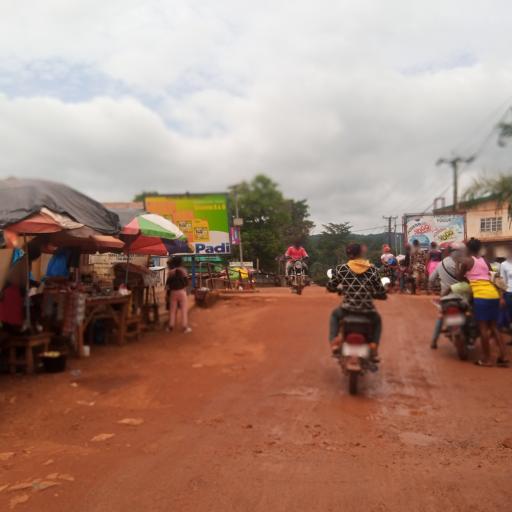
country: SL
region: Eastern Province
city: Kenema
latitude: 7.8765
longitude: -11.1938
